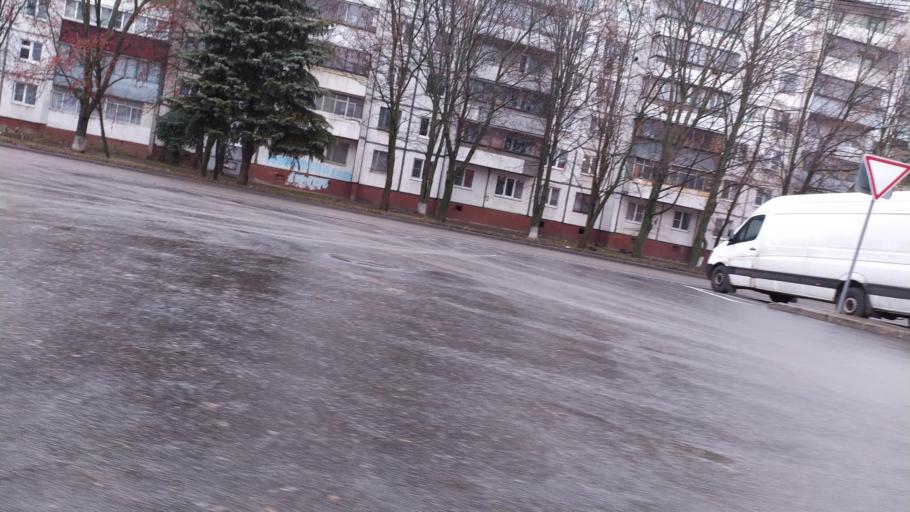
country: RU
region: Kursk
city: Kursk
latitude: 51.7424
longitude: 36.1347
